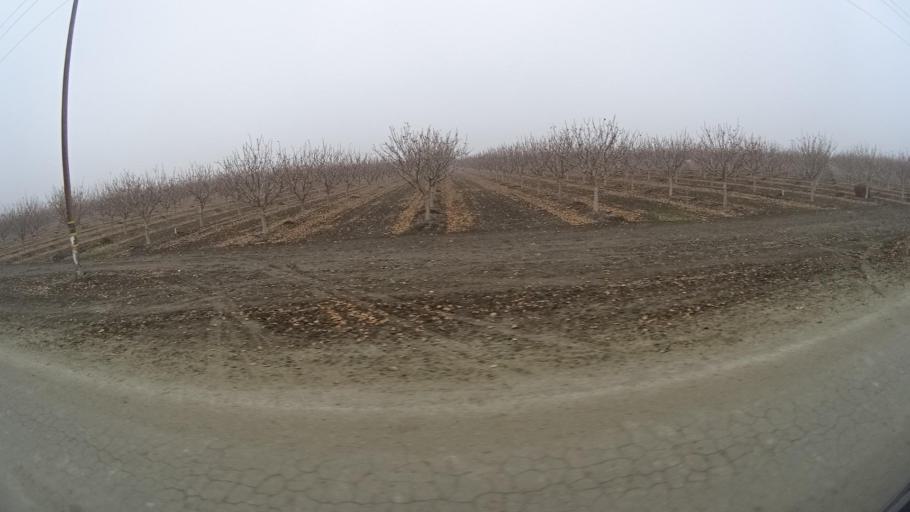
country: US
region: California
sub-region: Kern County
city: Buttonwillow
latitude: 35.4540
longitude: -119.5175
